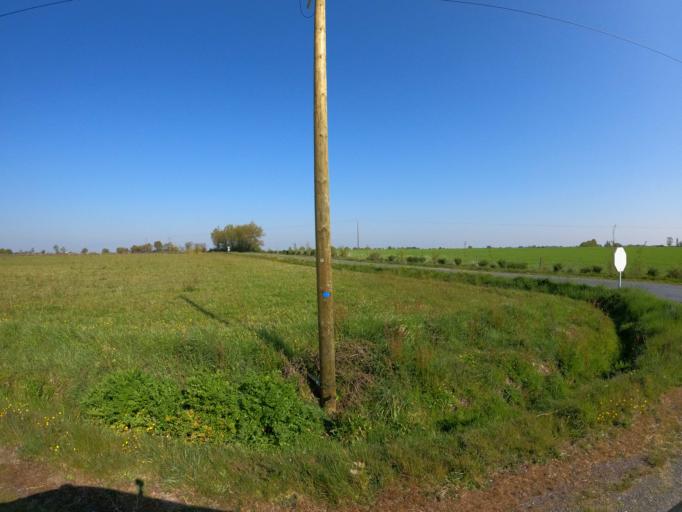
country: FR
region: Pays de la Loire
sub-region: Departement de la Loire-Atlantique
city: Aigrefeuille-sur-Maine
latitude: 47.0848
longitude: -1.4142
